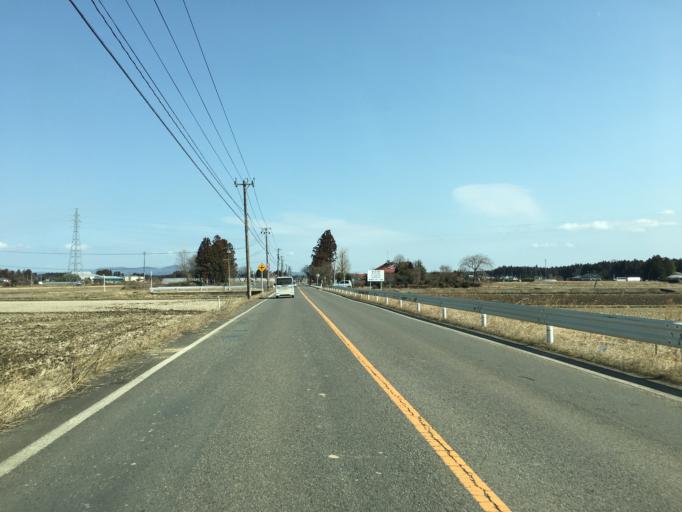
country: JP
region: Fukushima
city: Ishikawa
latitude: 37.1385
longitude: 140.3356
